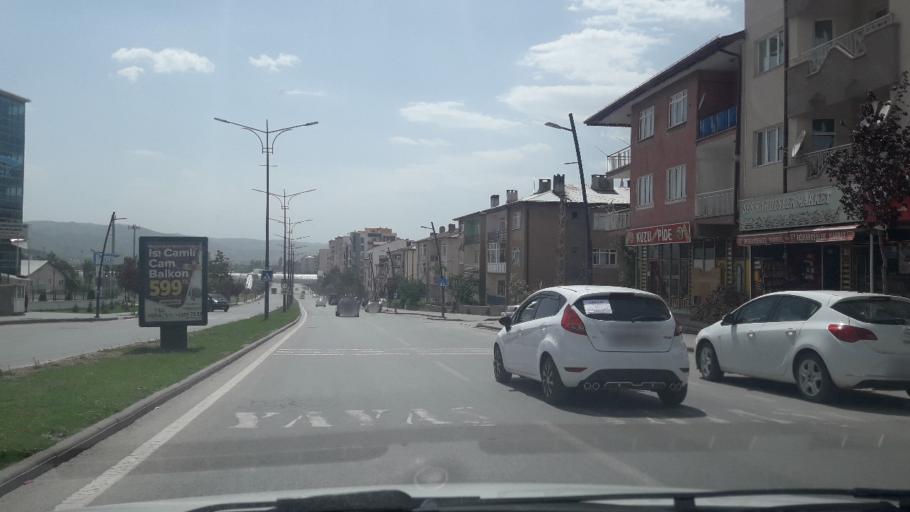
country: TR
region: Sivas
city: Sivas
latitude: 39.7327
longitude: 36.9870
